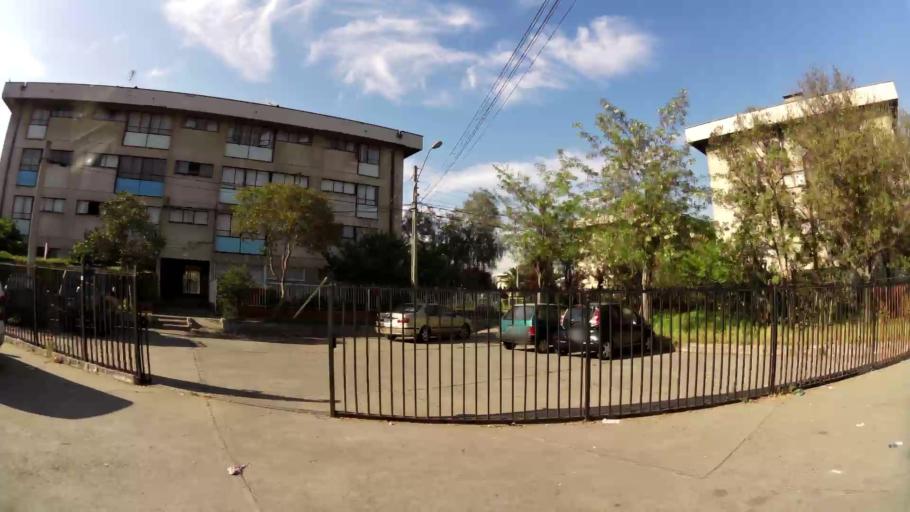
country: CL
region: Santiago Metropolitan
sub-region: Provincia de Santiago
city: La Pintana
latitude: -33.5633
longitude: -70.5938
